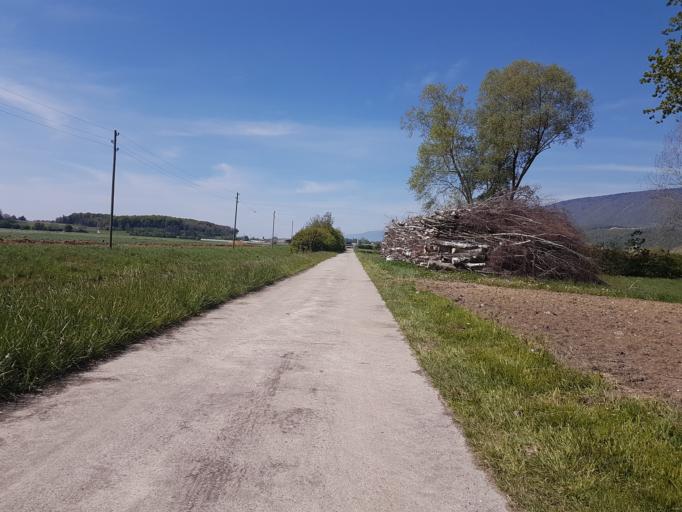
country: CH
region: Neuchatel
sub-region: Neuchatel District
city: Le Landeron
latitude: 47.0389
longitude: 7.0547
